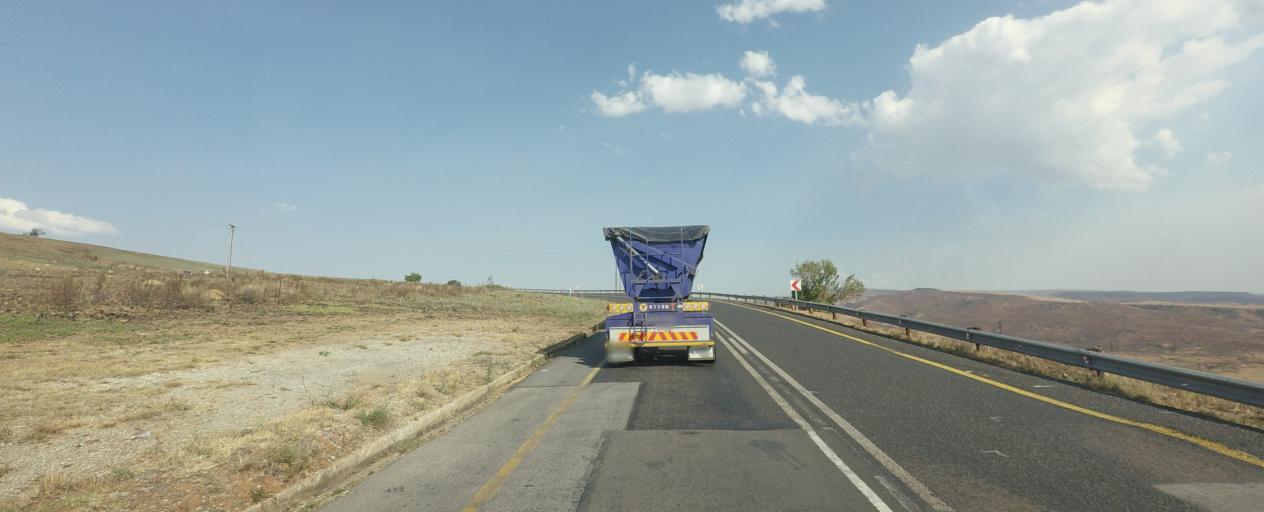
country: ZA
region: Mpumalanga
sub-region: Ehlanzeni District
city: Lydenburg
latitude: -25.1109
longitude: 30.4987
